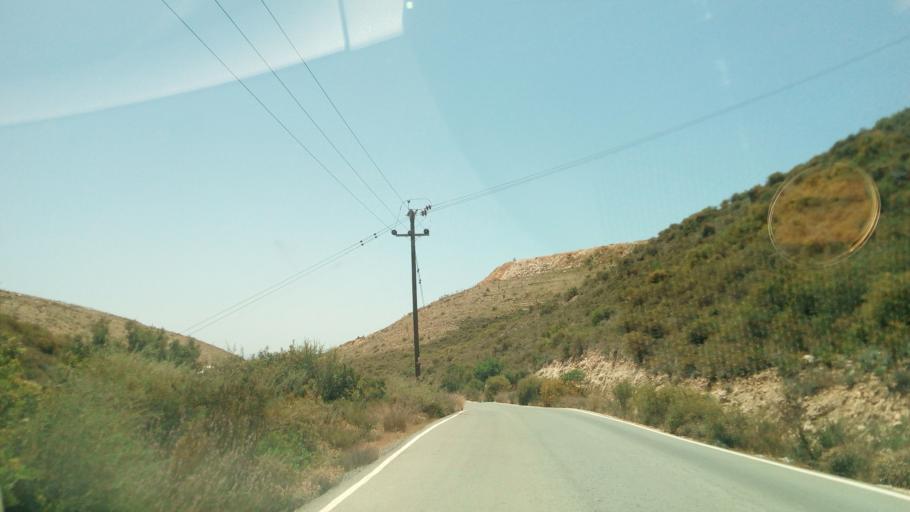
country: CY
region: Limassol
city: Ypsonas
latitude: 34.7342
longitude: 32.9477
